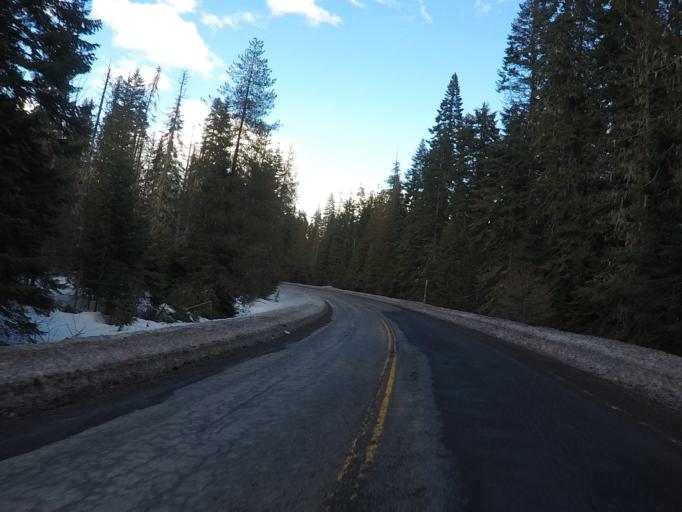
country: US
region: Montana
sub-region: Ravalli County
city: Hamilton
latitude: 46.5073
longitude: -114.7746
